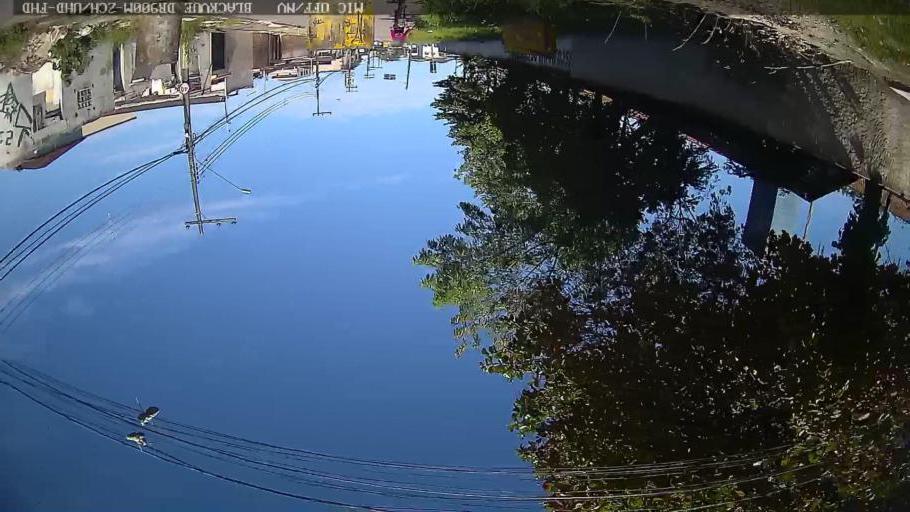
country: BR
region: Sao Paulo
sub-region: Guaruja
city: Guaruja
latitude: -23.9617
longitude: -46.2793
